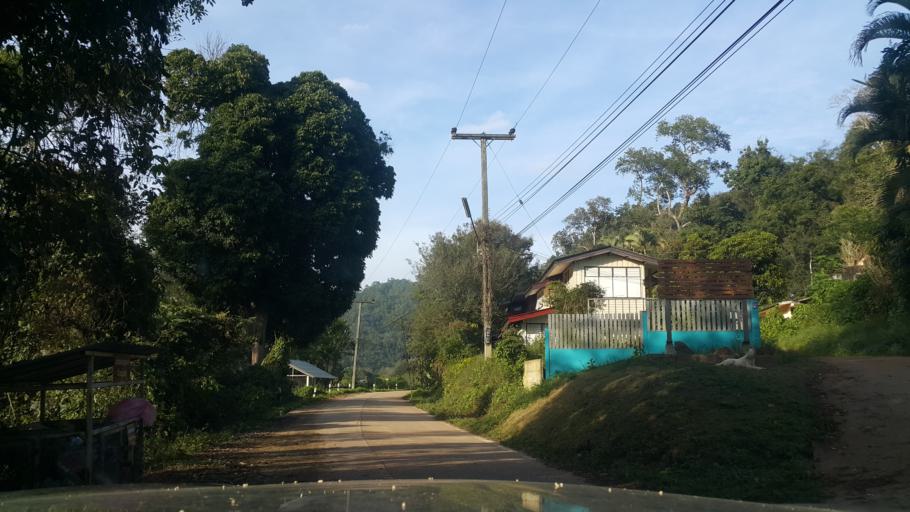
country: TH
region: Chiang Mai
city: Samoeng
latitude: 19.0128
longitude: 98.6731
